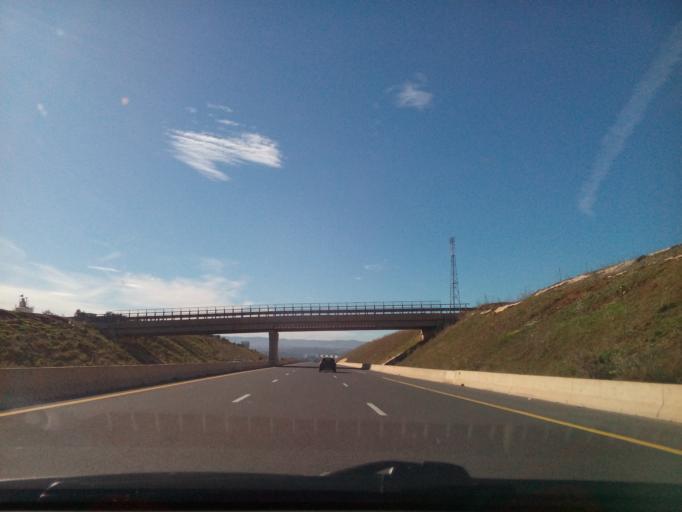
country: DZ
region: Tlemcen
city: Chetouane
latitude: 34.9700
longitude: -1.2637
